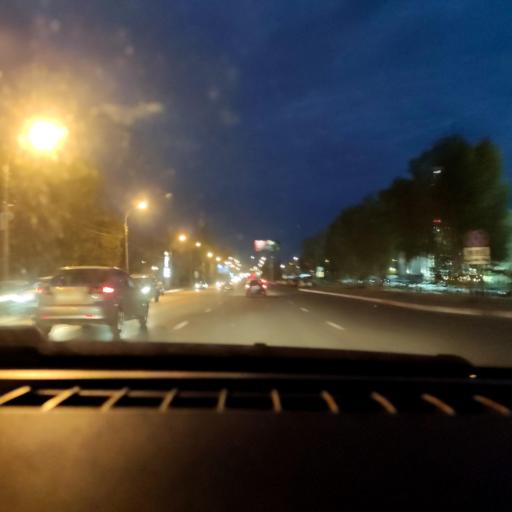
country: RU
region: Voronezj
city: Voronezh
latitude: 51.6546
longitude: 39.2912
